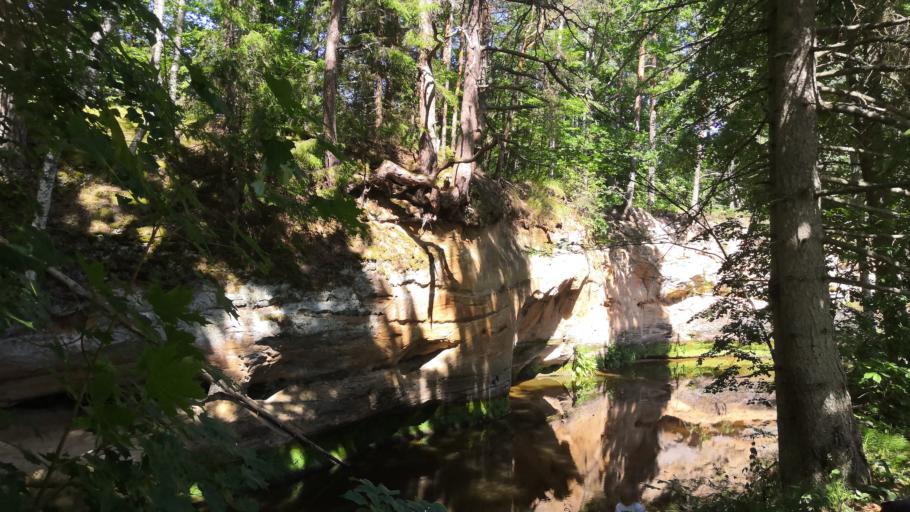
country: LV
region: Rojas
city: Roja
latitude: 57.4328
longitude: 22.7180
